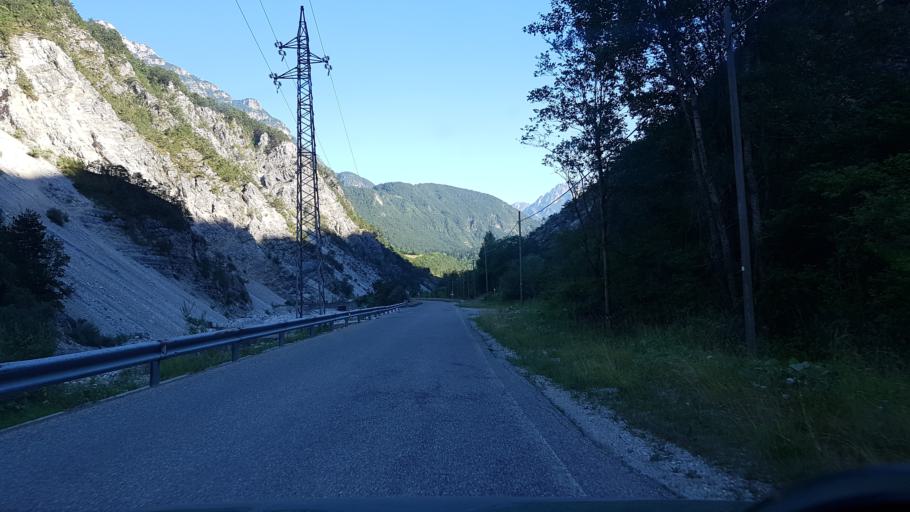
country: IT
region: Friuli Venezia Giulia
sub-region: Provincia di Udine
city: Moggio Udinese
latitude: 46.4405
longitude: 13.1950
